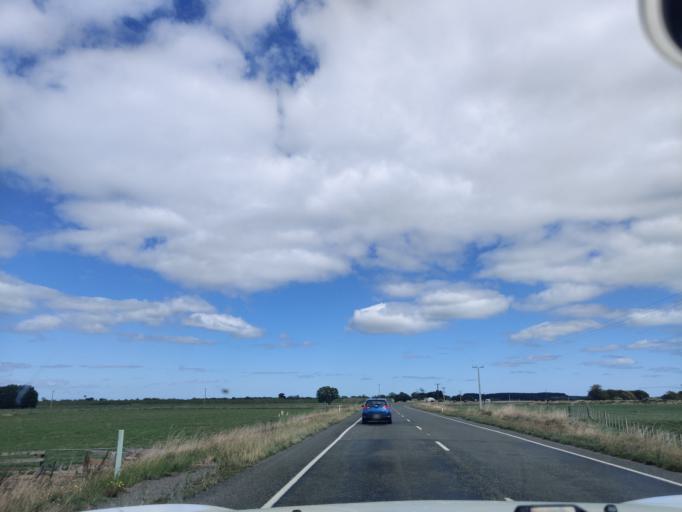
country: NZ
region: Manawatu-Wanganui
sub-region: Palmerston North City
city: Palmerston North
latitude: -40.4245
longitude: 175.4607
